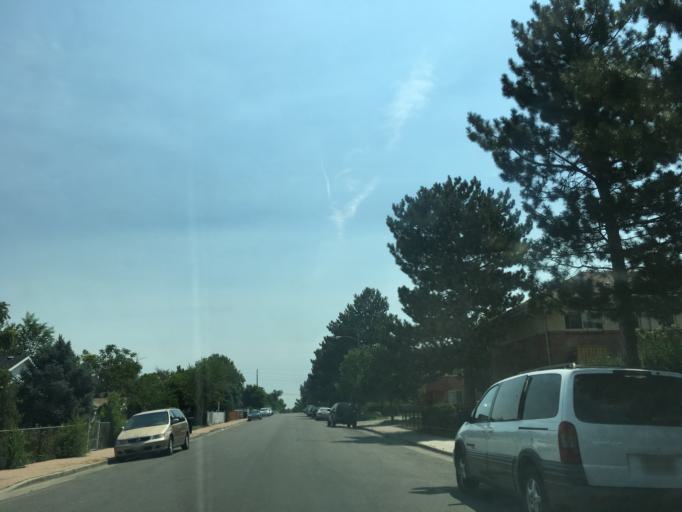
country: US
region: Colorado
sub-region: Jefferson County
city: Lakewood
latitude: 39.7022
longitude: -105.0319
